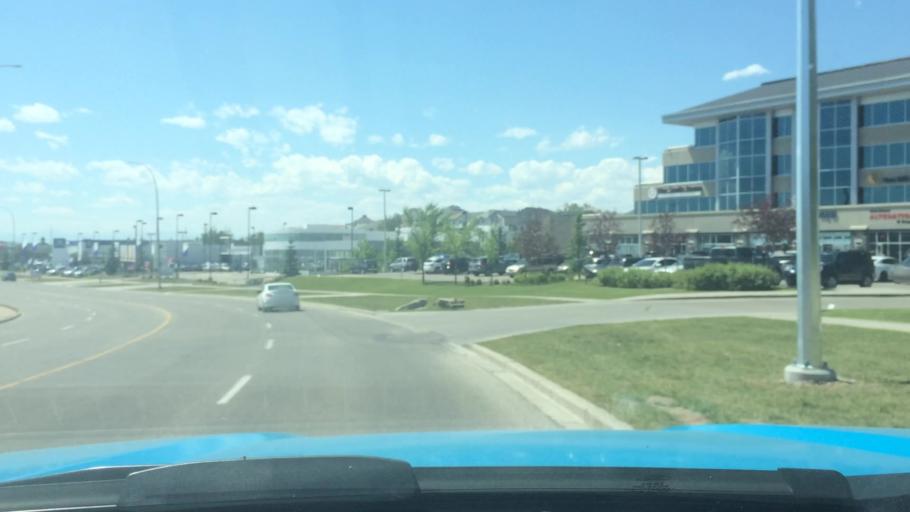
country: CA
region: Alberta
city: Calgary
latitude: 51.1292
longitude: -114.2030
